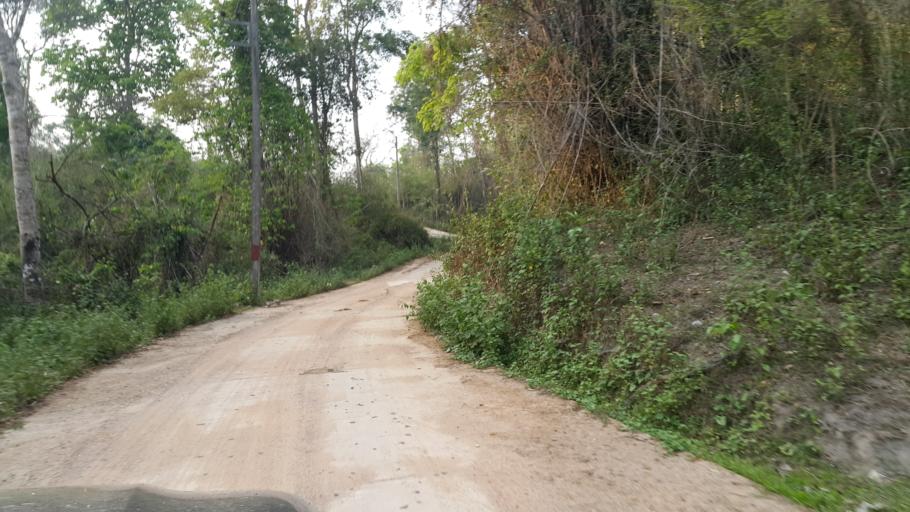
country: TH
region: Chiang Mai
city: Mae On
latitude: 18.7879
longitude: 99.2964
